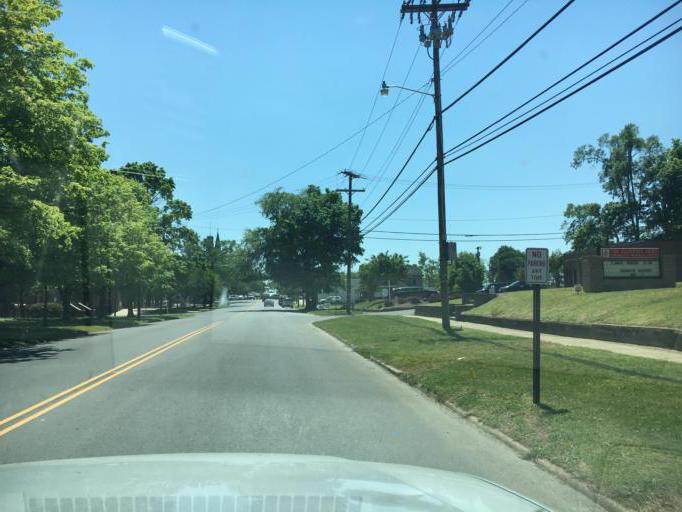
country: US
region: North Carolina
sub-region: Cleveland County
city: Shelby
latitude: 35.2953
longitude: -81.5401
